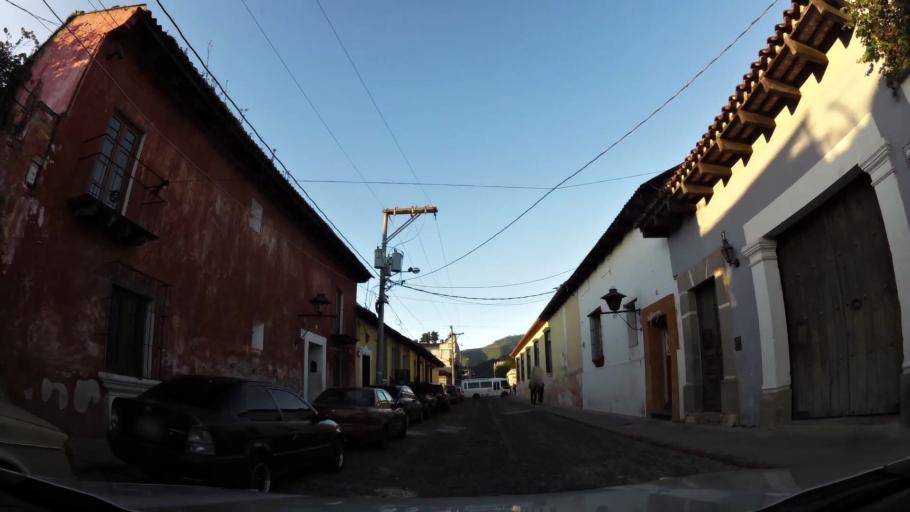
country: GT
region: Sacatepequez
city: Antigua Guatemala
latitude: 14.5548
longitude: -90.7342
